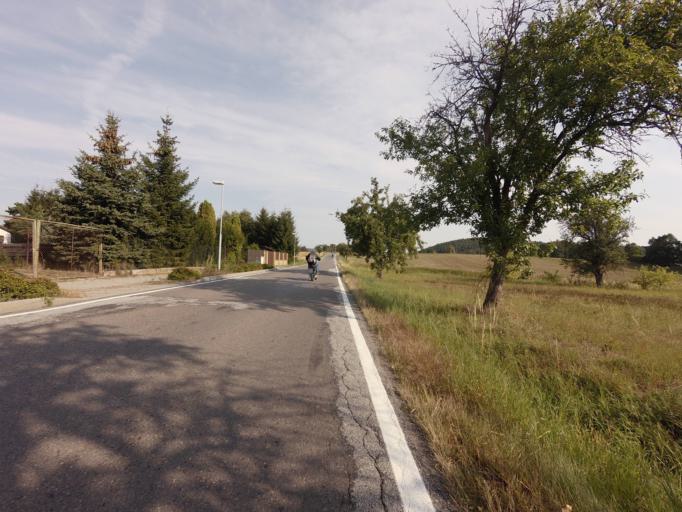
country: CZ
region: Jihocesky
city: Milevsko
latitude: 49.4630
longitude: 14.3627
